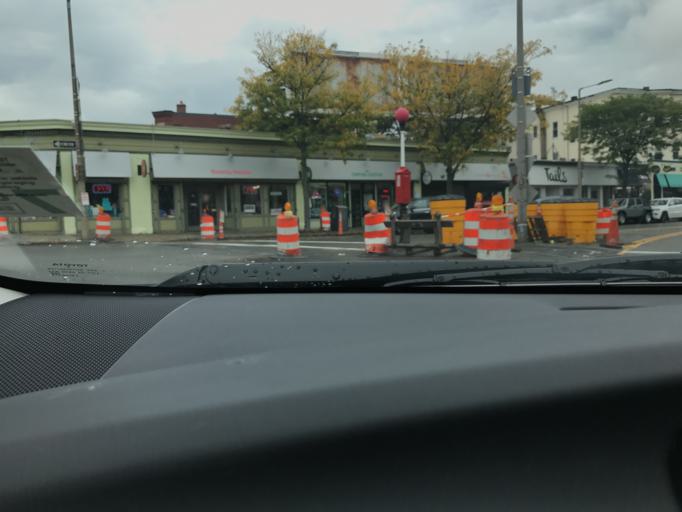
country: US
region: Massachusetts
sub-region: Norfolk County
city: Brookline
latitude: 42.3219
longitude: -71.1098
